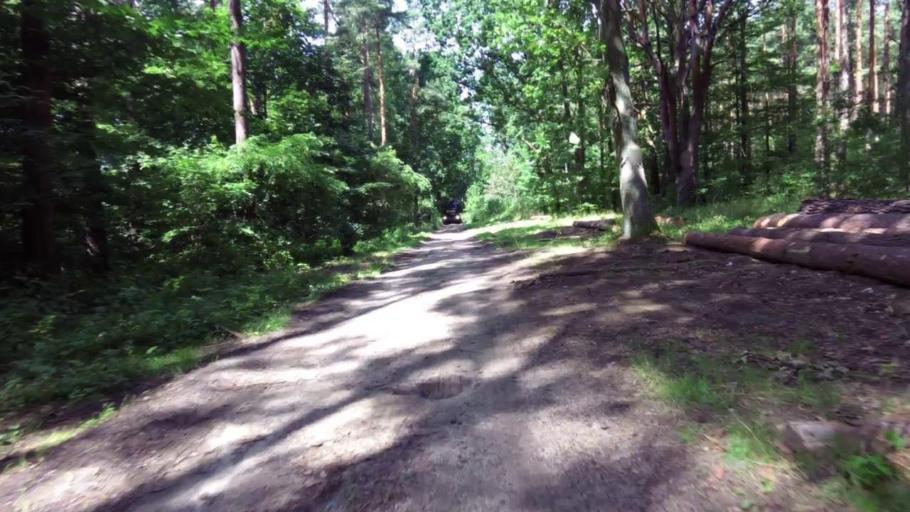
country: PL
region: West Pomeranian Voivodeship
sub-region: Powiat gryfinski
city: Stare Czarnowo
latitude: 53.3517
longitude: 14.7567
